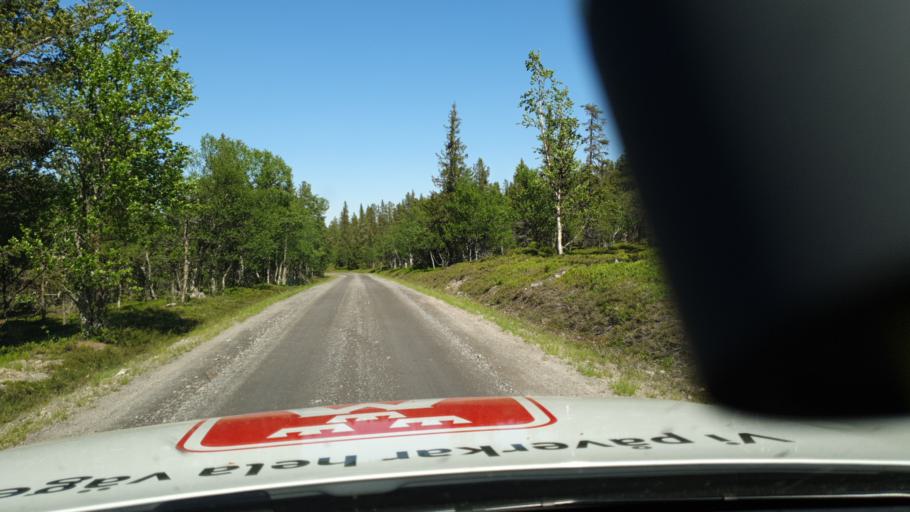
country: NO
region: Hedmark
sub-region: Engerdal
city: Engerdal
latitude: 62.1410
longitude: 12.9434
